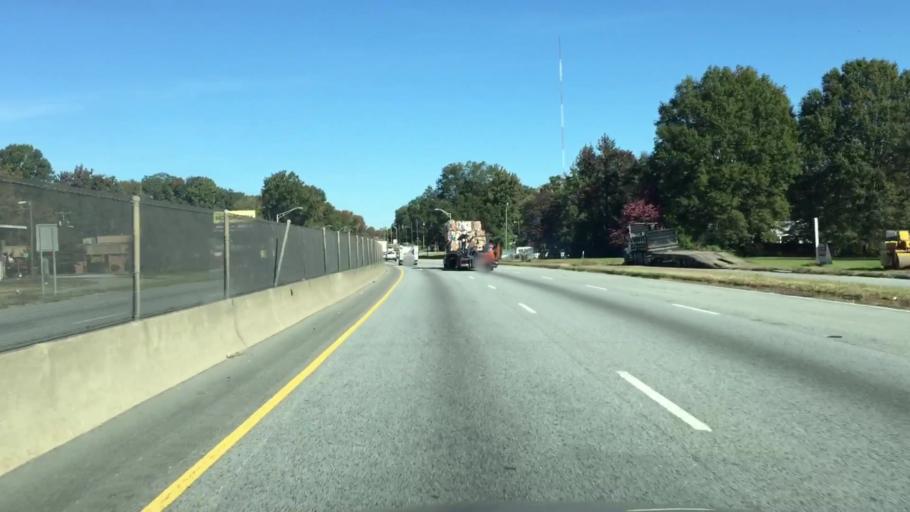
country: US
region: North Carolina
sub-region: Guilford County
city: Greensboro
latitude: 36.0910
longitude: -79.7657
